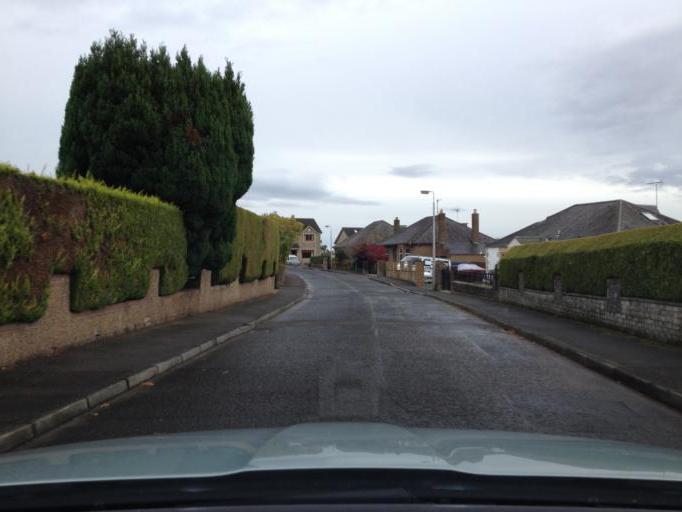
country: GB
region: Scotland
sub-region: Perth and Kinross
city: Crieff
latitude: 56.3727
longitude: -3.8329
